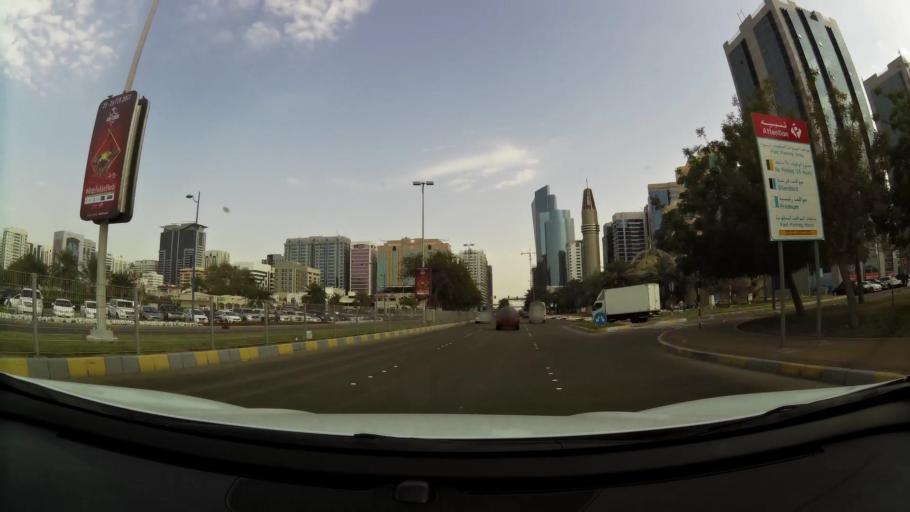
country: AE
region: Abu Dhabi
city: Abu Dhabi
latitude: 24.4778
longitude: 54.3462
